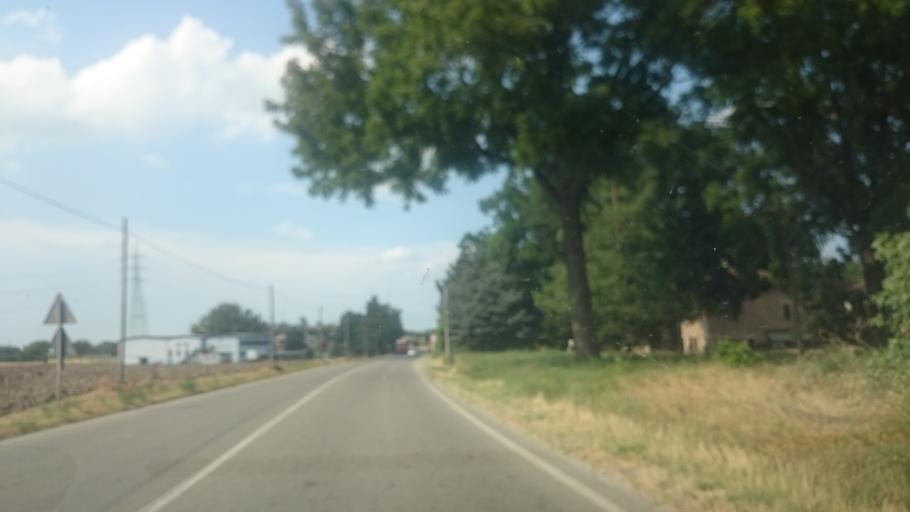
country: IT
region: Emilia-Romagna
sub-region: Provincia di Reggio Emilia
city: Rubiera
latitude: 44.6305
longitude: 10.7776
